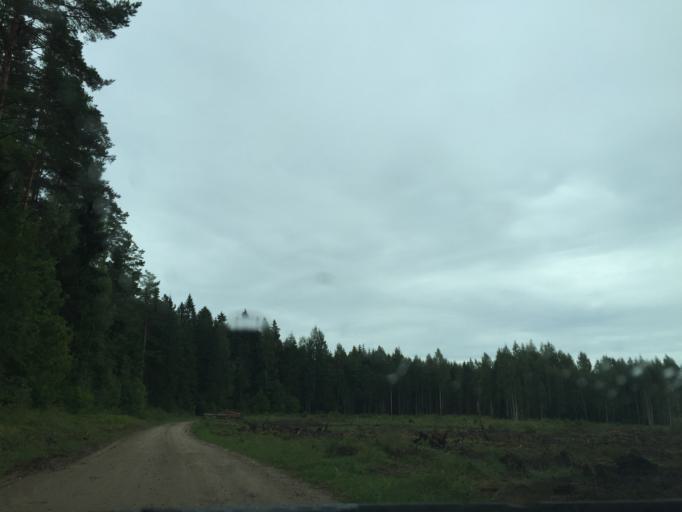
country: LV
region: Preilu Rajons
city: Jaunaglona
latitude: 56.2564
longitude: 27.1420
